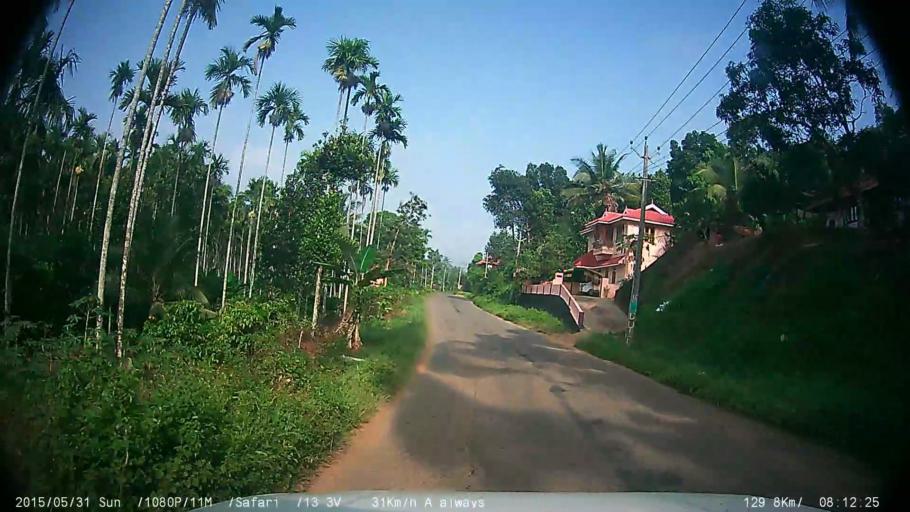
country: IN
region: Kerala
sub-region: Wayanad
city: Kalpetta
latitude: 11.6369
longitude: 76.0138
